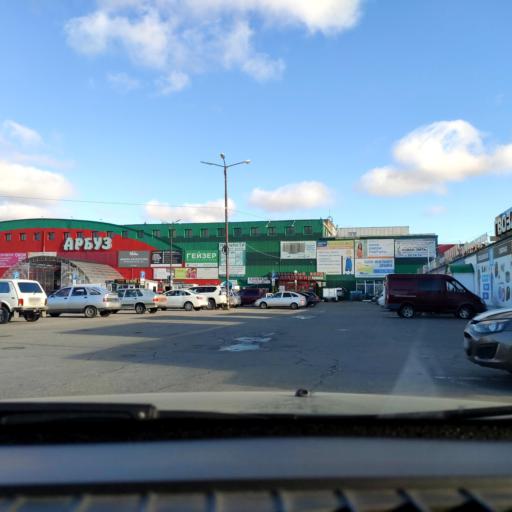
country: RU
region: Samara
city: Tol'yatti
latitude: 53.5600
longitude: 49.3075
